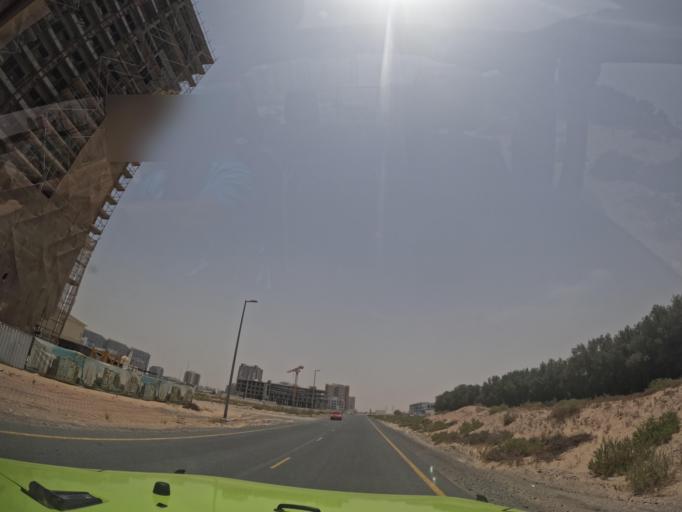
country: AE
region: Dubai
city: Dubai
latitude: 25.0924
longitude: 55.3741
